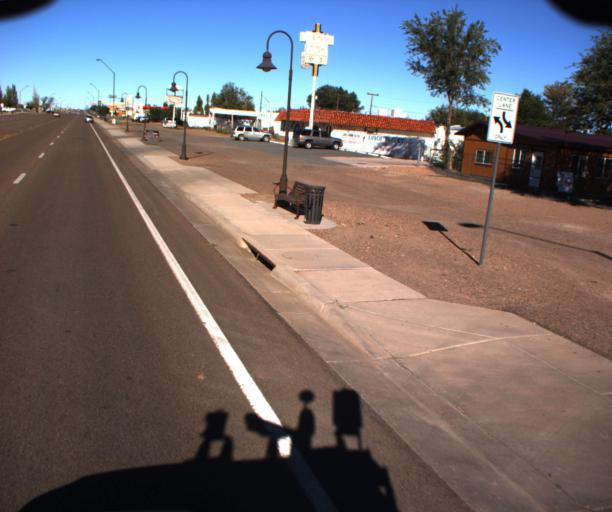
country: US
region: Arizona
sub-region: Navajo County
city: Holbrook
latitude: 34.9274
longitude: -110.1421
